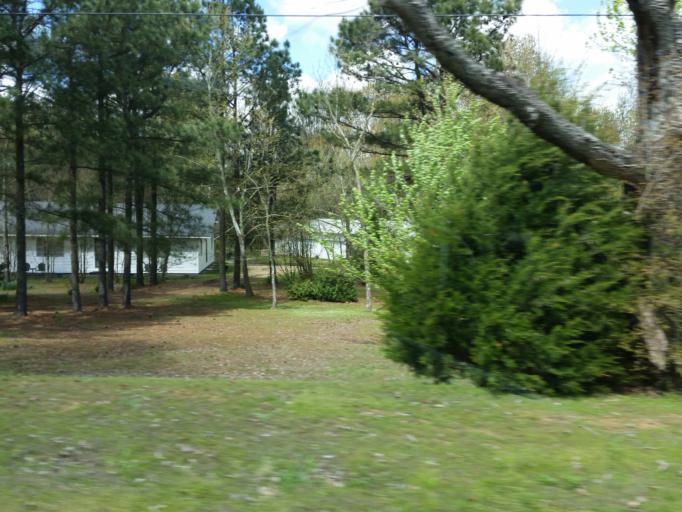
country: US
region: Arkansas
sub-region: Craighead County
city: Brookland
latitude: 36.0349
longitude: -90.6755
